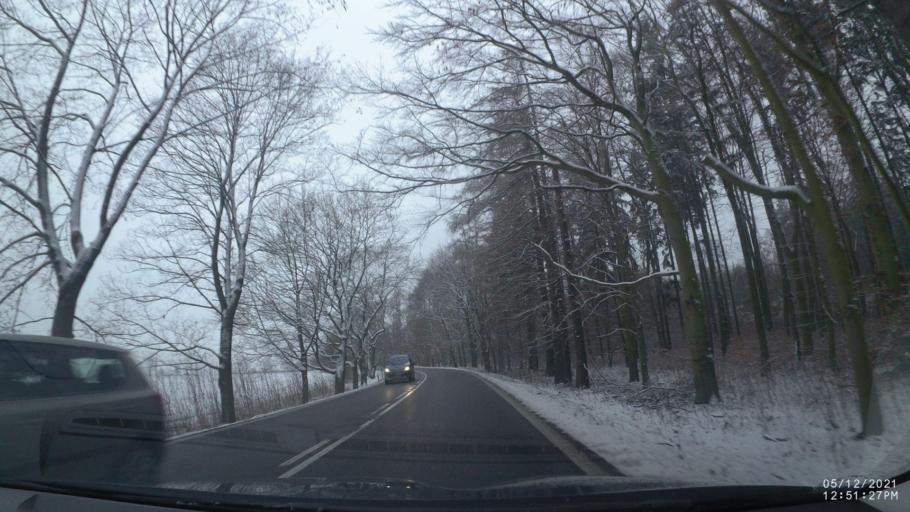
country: CZ
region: Kralovehradecky
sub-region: Okres Nachod
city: Nachod
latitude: 50.3970
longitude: 16.1383
